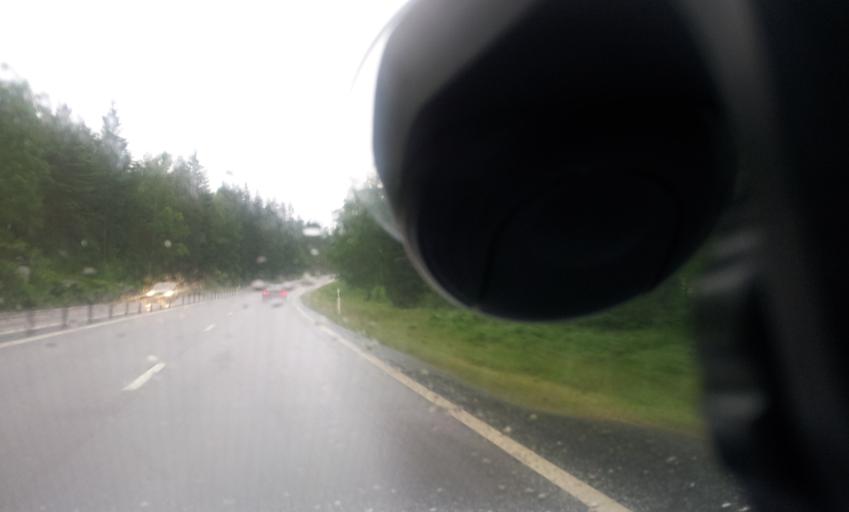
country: SE
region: Kalmar
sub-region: Vasterviks Kommun
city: Forserum
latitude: 58.0330
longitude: 16.5152
